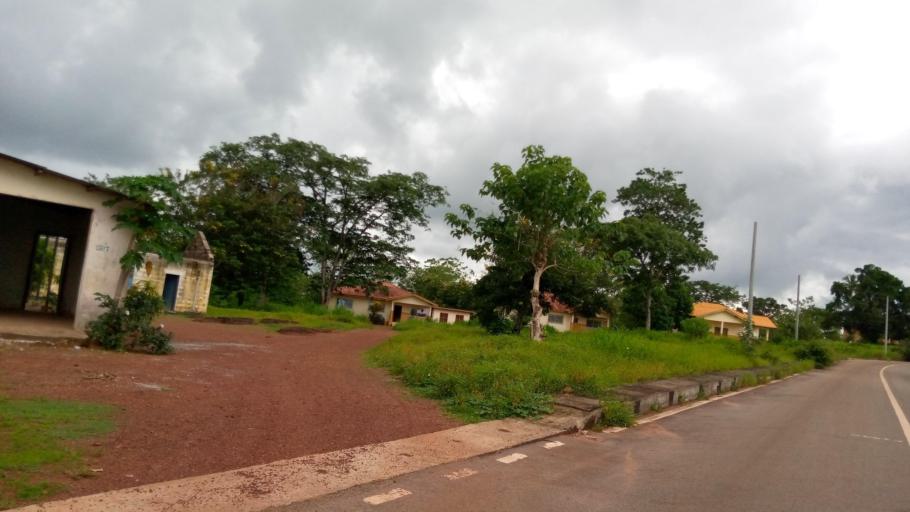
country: SL
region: Southern Province
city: Moyamba
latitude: 8.1606
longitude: -12.4421
